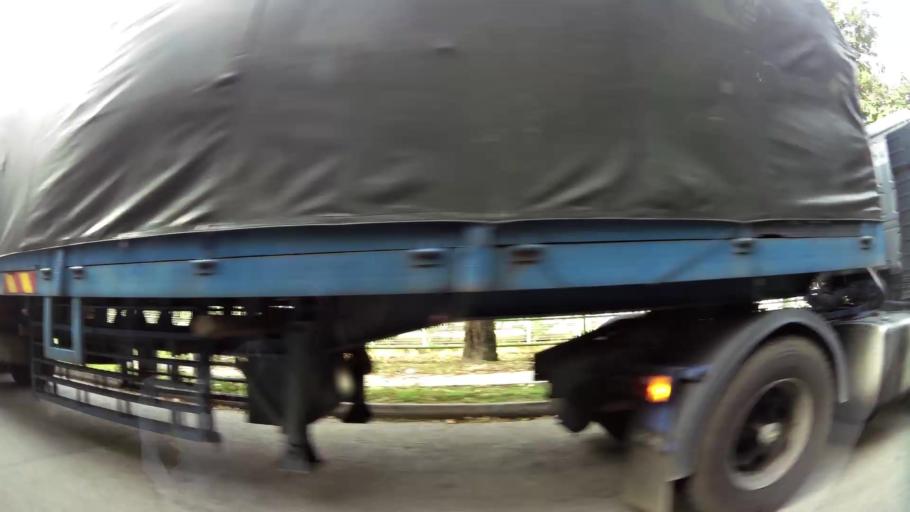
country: MY
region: Johor
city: Johor Bahru
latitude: 1.3329
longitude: 103.6492
